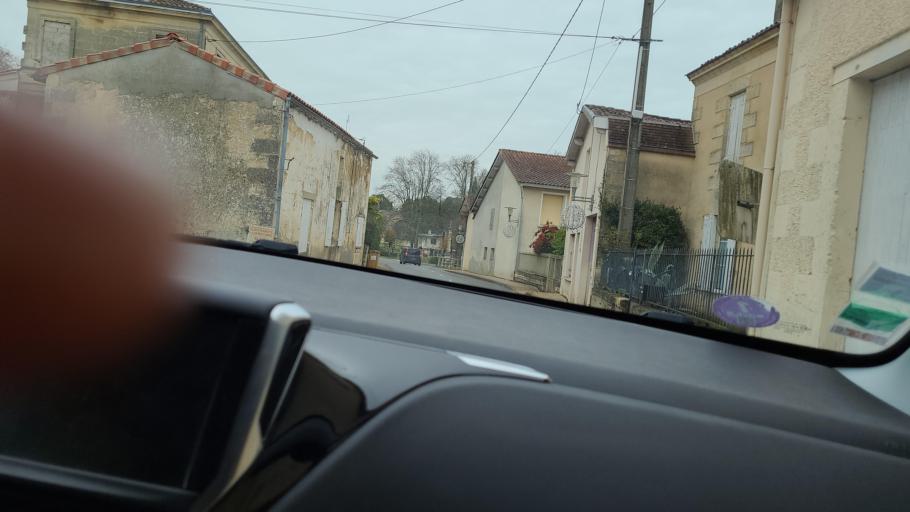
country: FR
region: Aquitaine
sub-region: Departement de la Gironde
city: Berson
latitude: 45.0920
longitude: -0.5479
